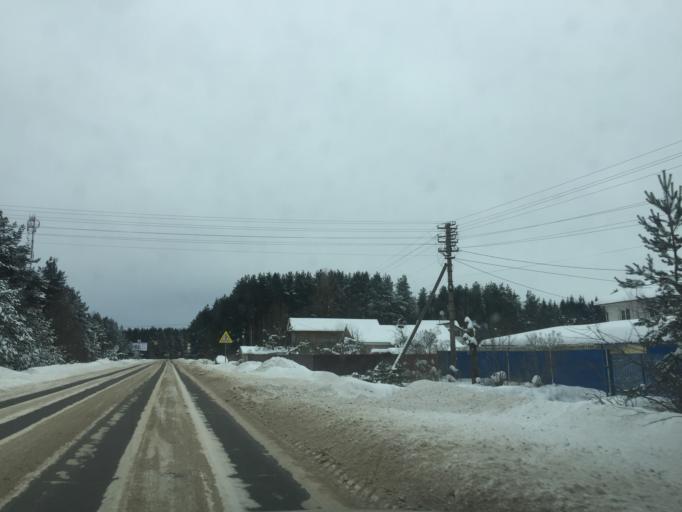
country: RU
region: Leningrad
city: Imeni Sverdlova
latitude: 59.8617
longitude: 30.6713
